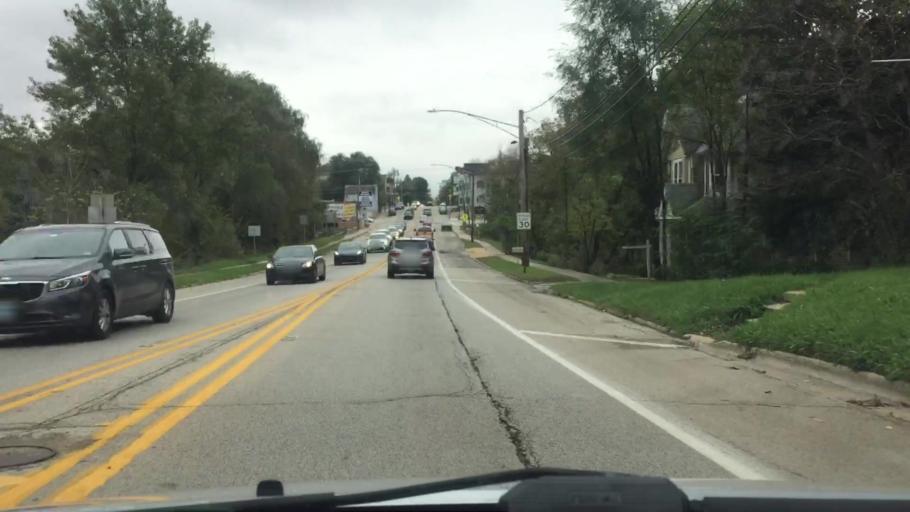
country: US
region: Illinois
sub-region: McHenry County
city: Richmond
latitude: 42.4785
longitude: -88.3061
